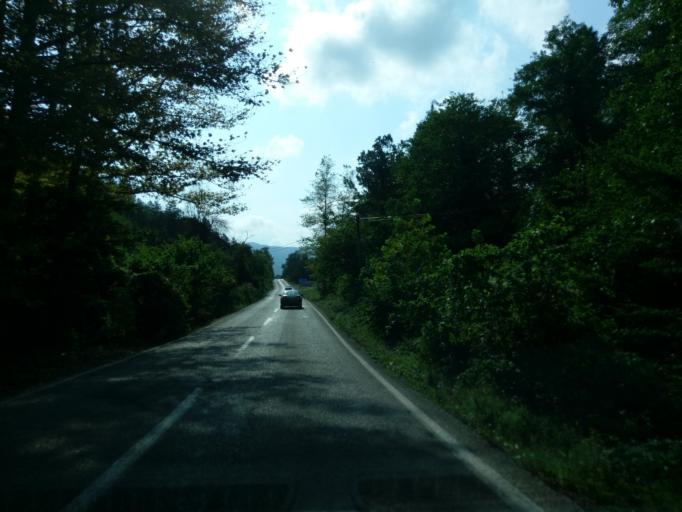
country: TR
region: Sinop
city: Ayancik
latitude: 41.8819
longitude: 34.5233
